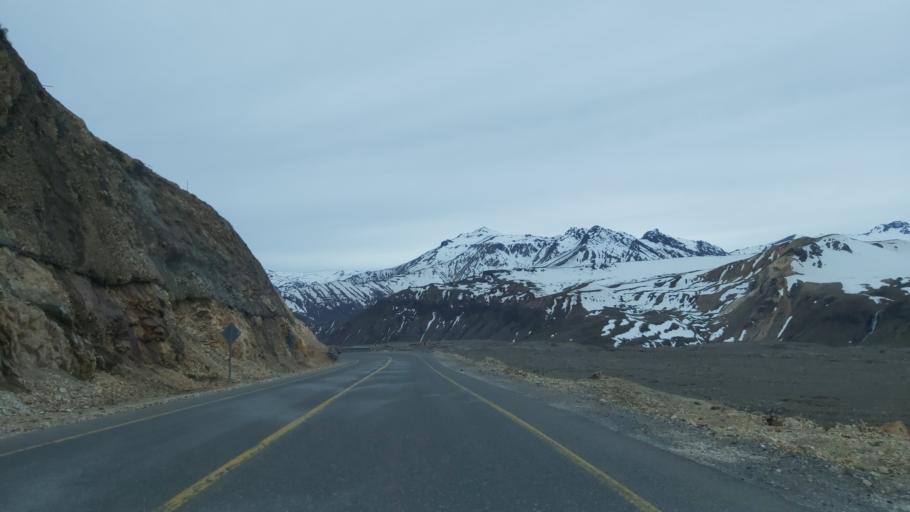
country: CL
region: Maule
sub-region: Provincia de Linares
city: Colbun
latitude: -35.9740
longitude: -70.5638
